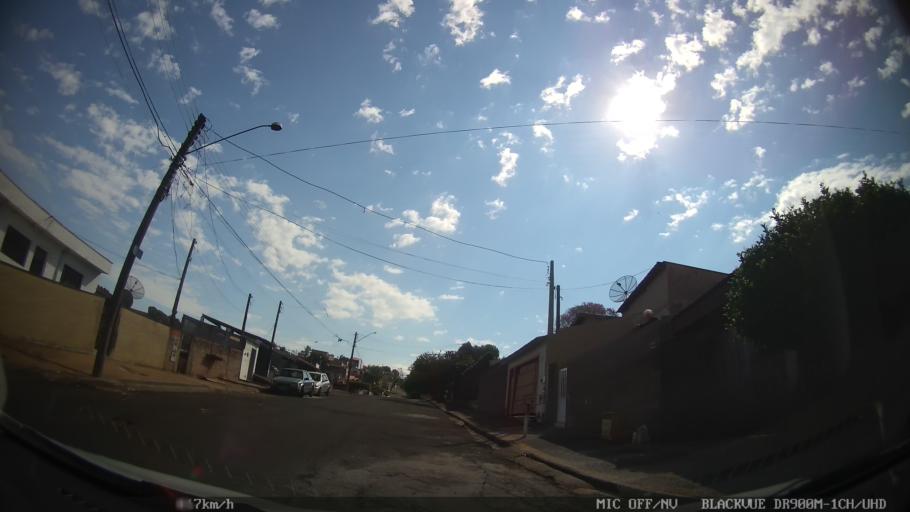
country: BR
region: Sao Paulo
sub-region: Nova Odessa
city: Nova Odessa
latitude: -22.7448
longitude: -47.2981
